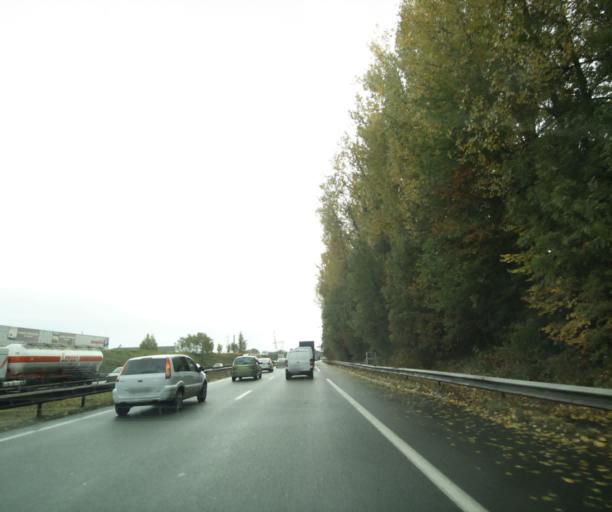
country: FR
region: Nord-Pas-de-Calais
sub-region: Departement du Nord
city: Mouvaux
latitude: 50.7123
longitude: 3.1232
